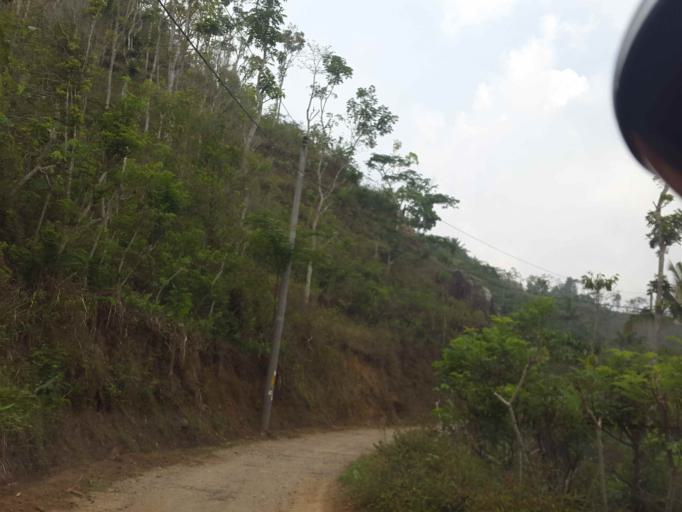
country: ID
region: East Java
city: Ploso
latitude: -8.0337
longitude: 111.1320
